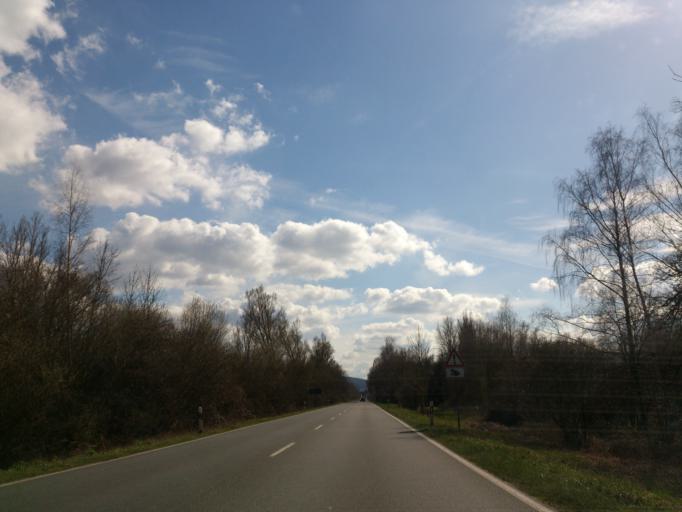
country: DE
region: Lower Saxony
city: Boffzen
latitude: 51.7490
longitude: 9.3697
